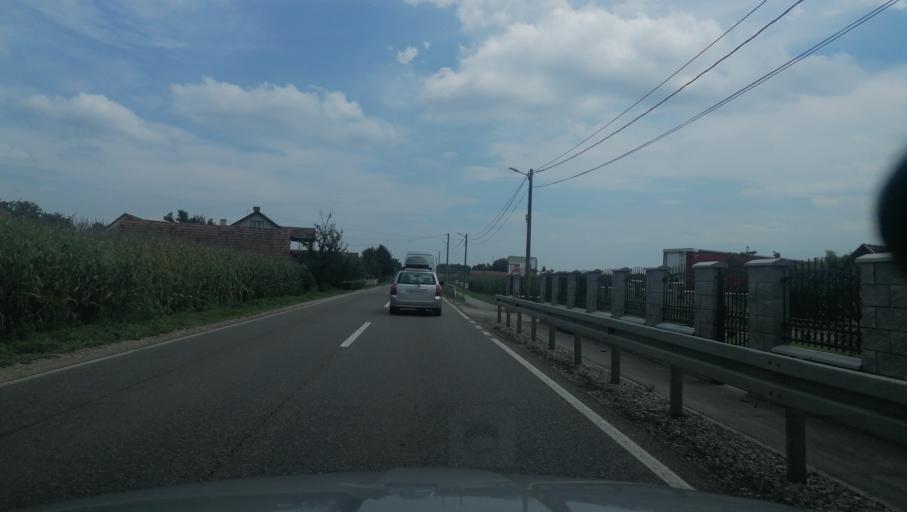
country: BA
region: Republika Srpska
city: Obudovac
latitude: 44.9575
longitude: 18.6318
